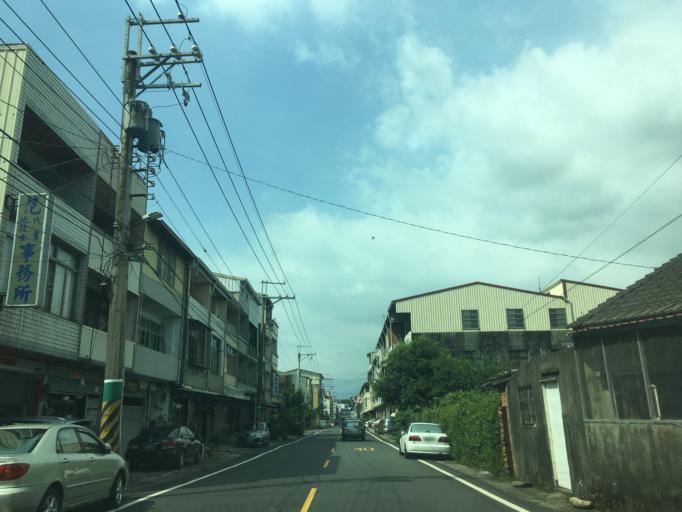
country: TW
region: Taiwan
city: Fengyuan
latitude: 24.2263
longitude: 120.7976
